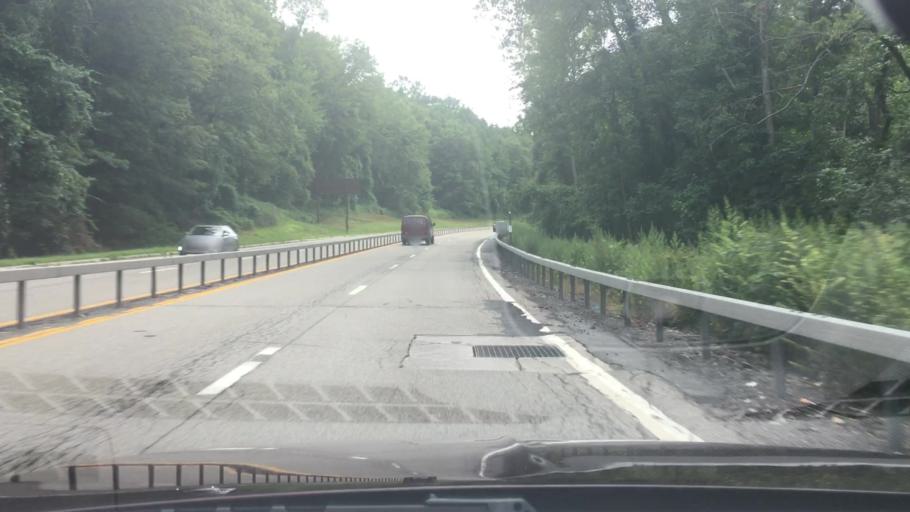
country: US
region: New York
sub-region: Putnam County
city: Mahopac
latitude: 41.4073
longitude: -73.7870
